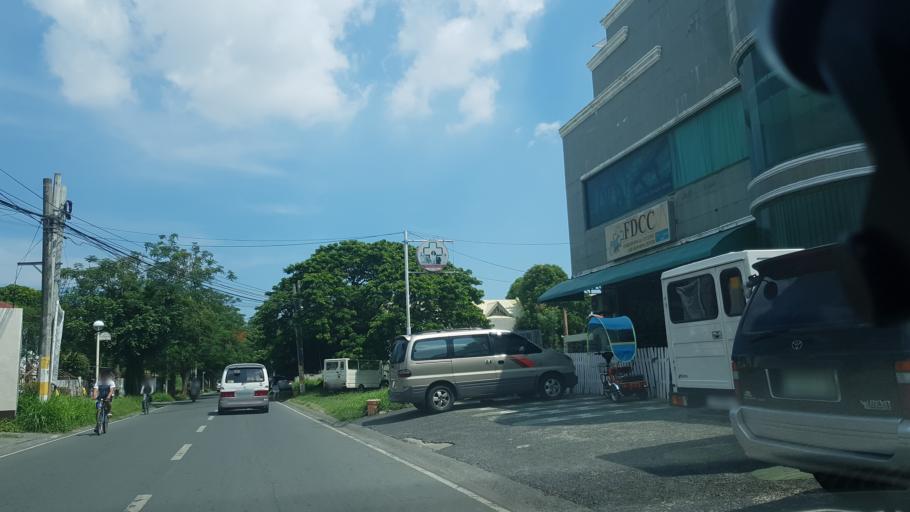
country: PH
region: Calabarzon
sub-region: Province of Rizal
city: Las Pinas
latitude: 14.4267
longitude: 120.9947
